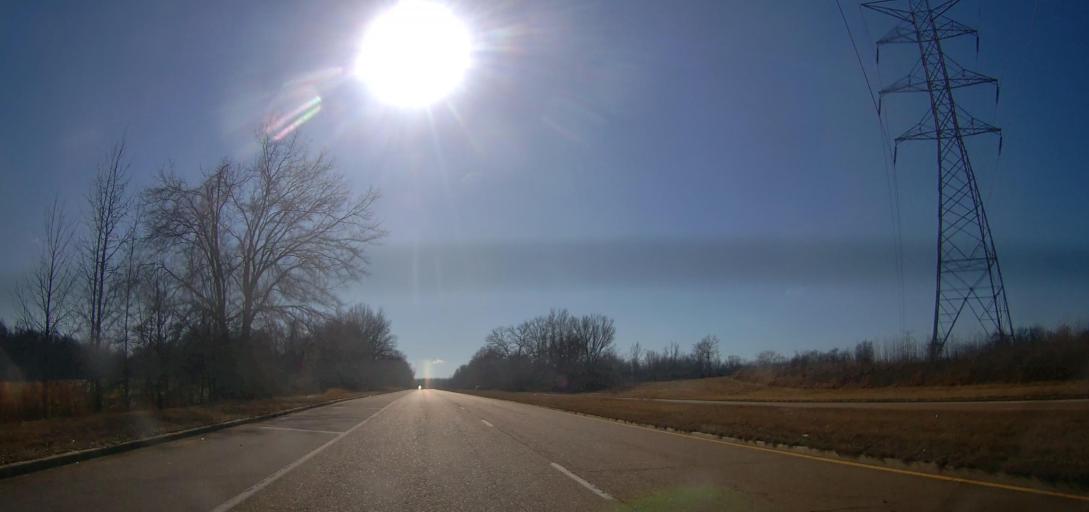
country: US
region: Tennessee
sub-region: Shelby County
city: Bartlett
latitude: 35.2530
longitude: -89.8942
